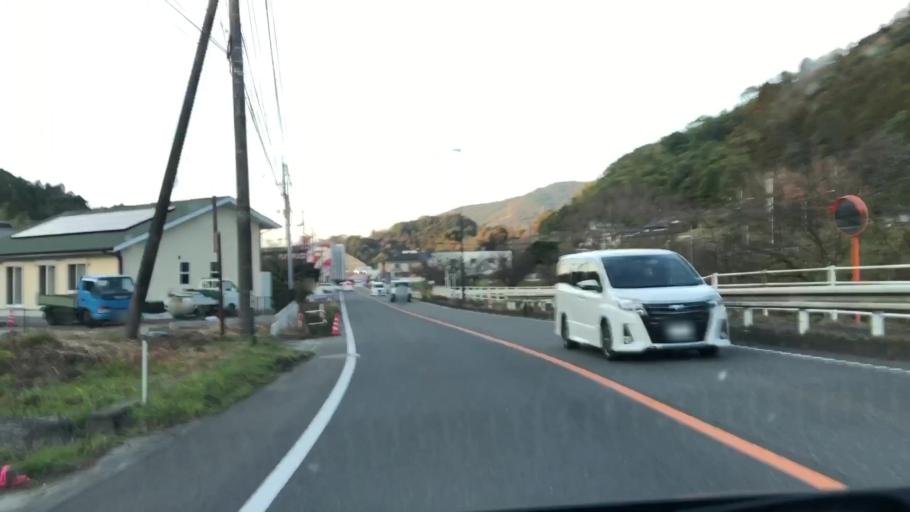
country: JP
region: Kumamoto
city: Minamata
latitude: 32.2200
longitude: 130.4383
